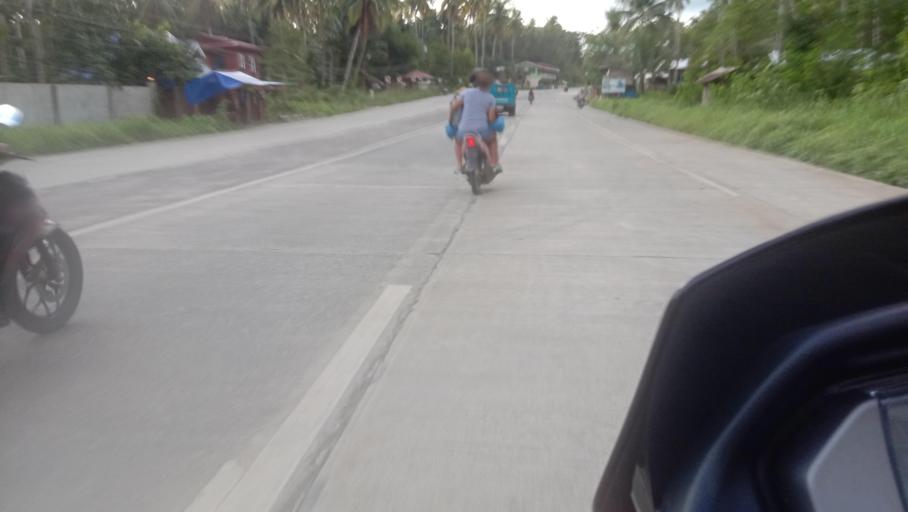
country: PH
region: Caraga
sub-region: Province of Surigao del Sur
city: Barobo
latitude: 8.5181
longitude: 126.1227
